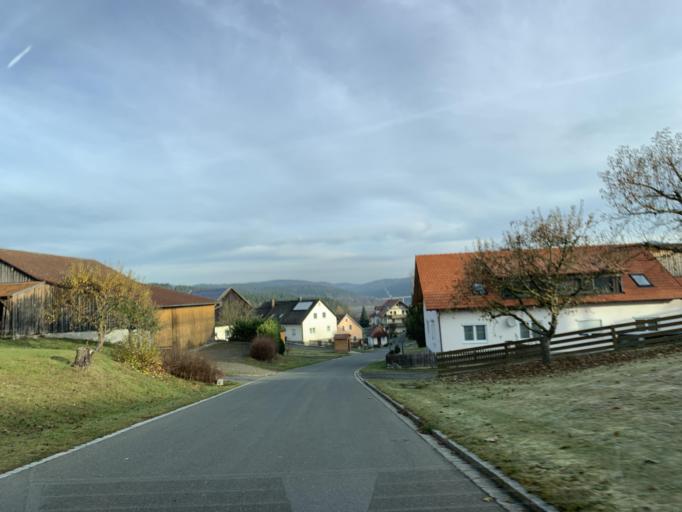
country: DE
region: Bavaria
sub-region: Upper Palatinate
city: Neukirchen-Balbini
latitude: 49.3340
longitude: 12.4396
